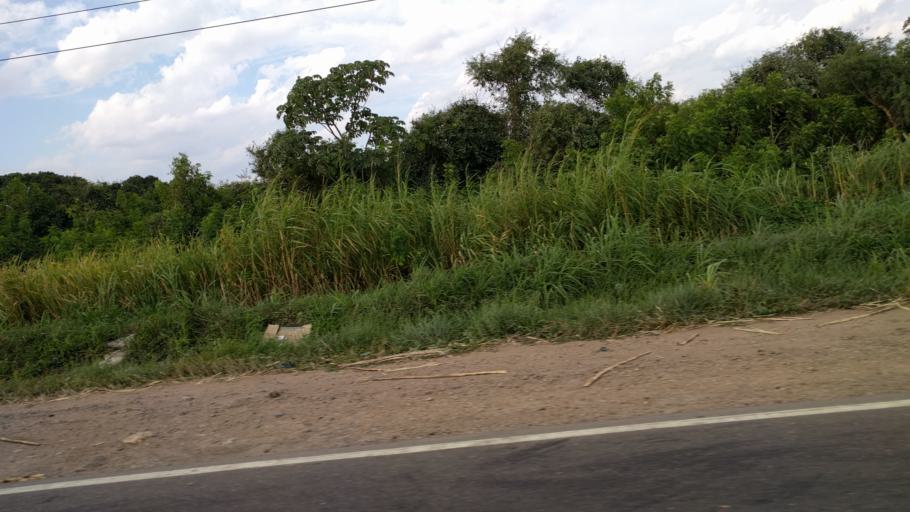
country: BO
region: Santa Cruz
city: Warnes
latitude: -17.5442
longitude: -63.1604
